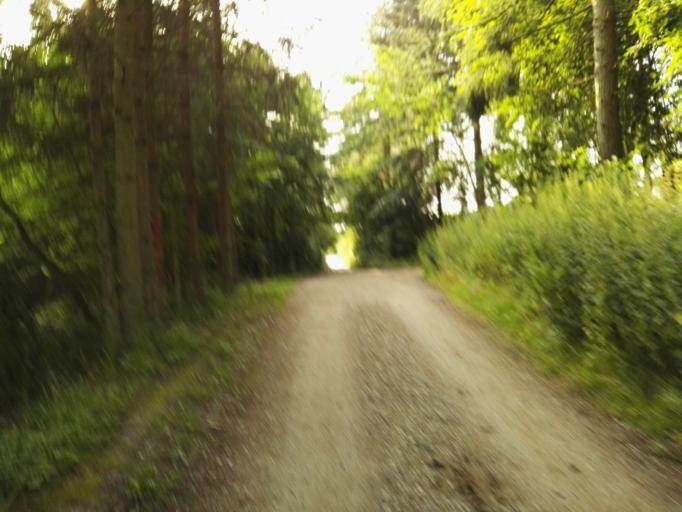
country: DK
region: Capital Region
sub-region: Ballerup Kommune
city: Ballerup
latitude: 55.7495
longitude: 12.3617
